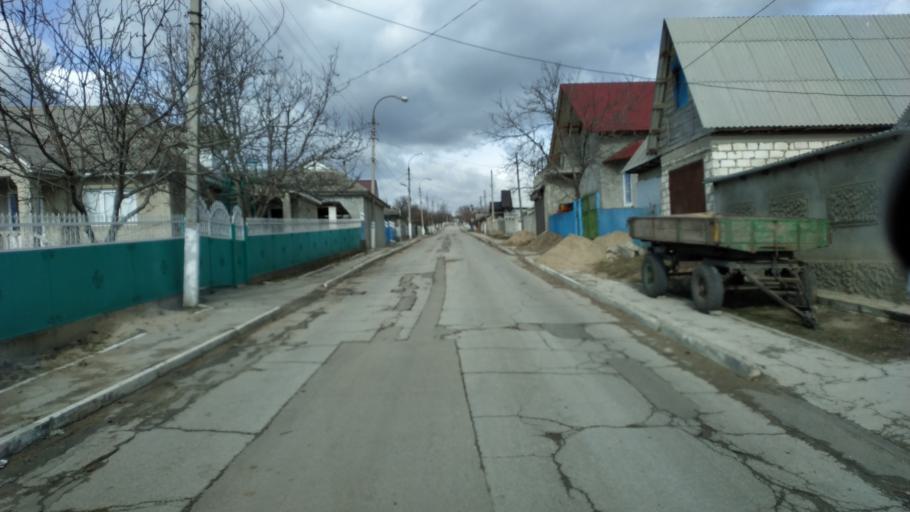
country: MD
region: Stinga Nistrului
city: Bucovat
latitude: 47.2058
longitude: 28.4970
